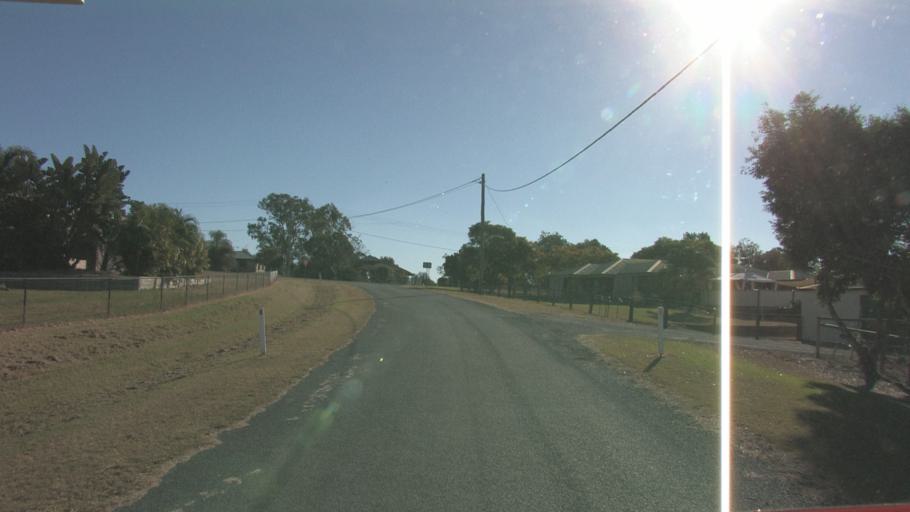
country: AU
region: Queensland
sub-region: Logan
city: North Maclean
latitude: -27.7886
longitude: 153.0258
